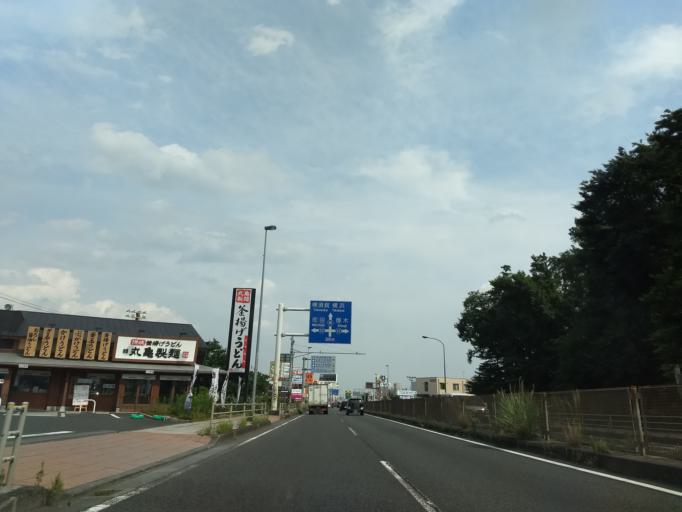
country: JP
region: Tokyo
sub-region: Machida-shi
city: Machida
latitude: 35.5450
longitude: 139.4274
